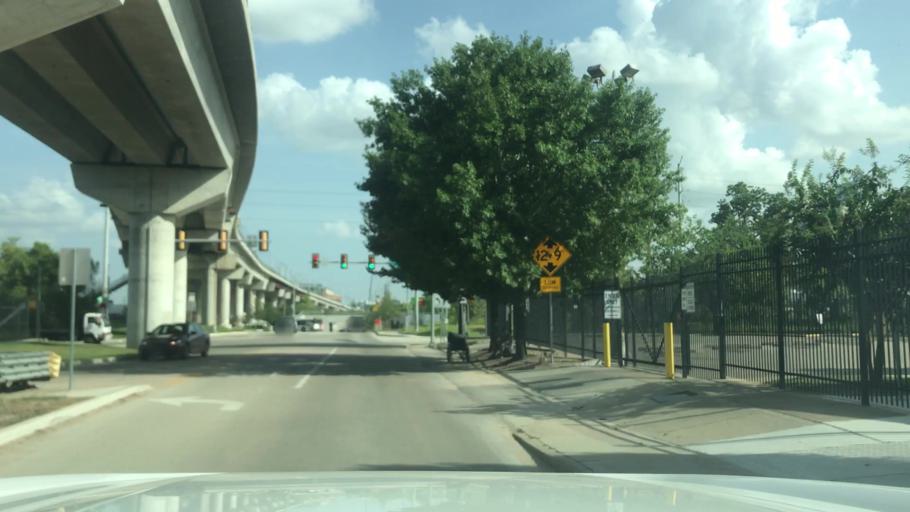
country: US
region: Texas
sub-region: Harris County
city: Houston
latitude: 29.7739
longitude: -95.3607
